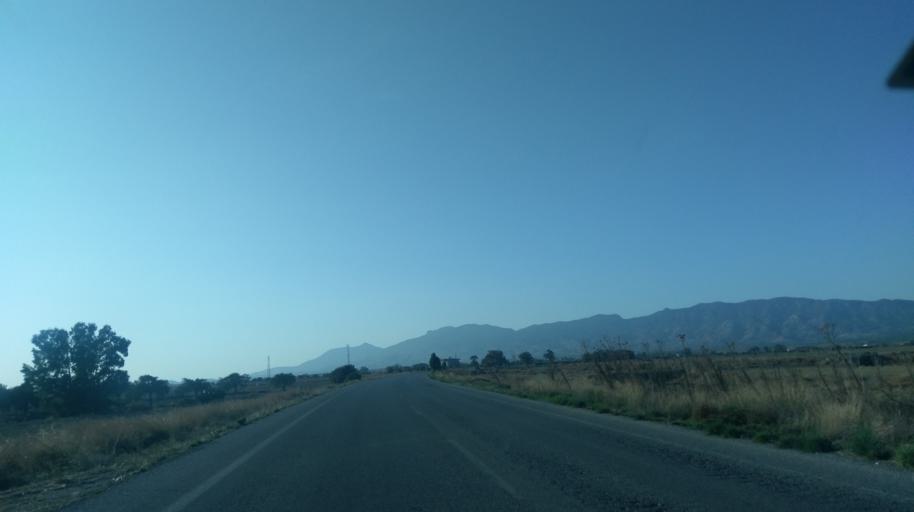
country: CY
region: Ammochostos
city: Lefkonoiko
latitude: 35.2584
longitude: 33.6748
